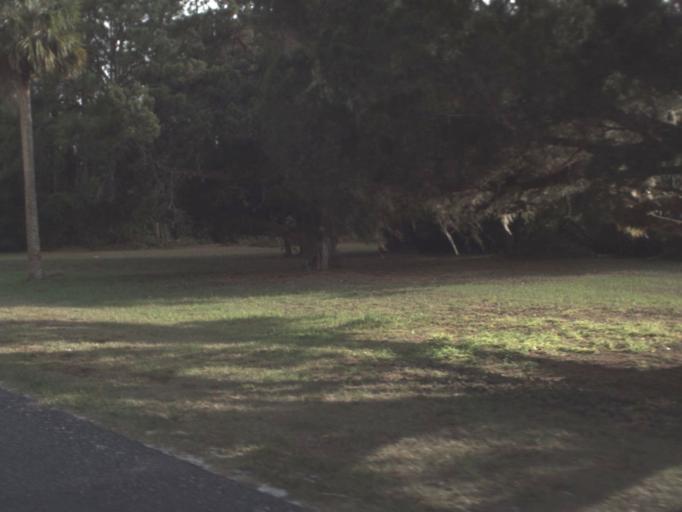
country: US
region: Florida
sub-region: Brevard County
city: Mims
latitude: 28.7189
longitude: -80.8634
